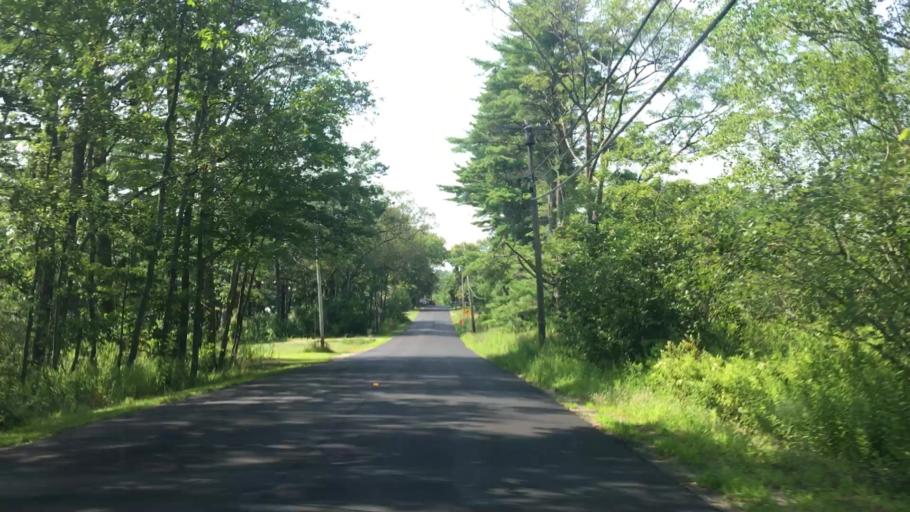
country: US
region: Maine
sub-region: Sagadahoc County
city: North Bath
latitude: 43.9460
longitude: -69.8056
